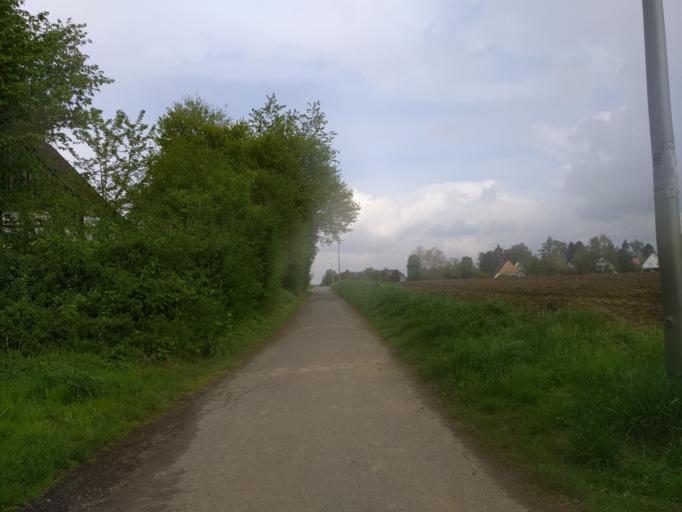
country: DE
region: North Rhine-Westphalia
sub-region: Regierungsbezirk Detmold
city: Bielefeld
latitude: 52.0524
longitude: 8.5049
